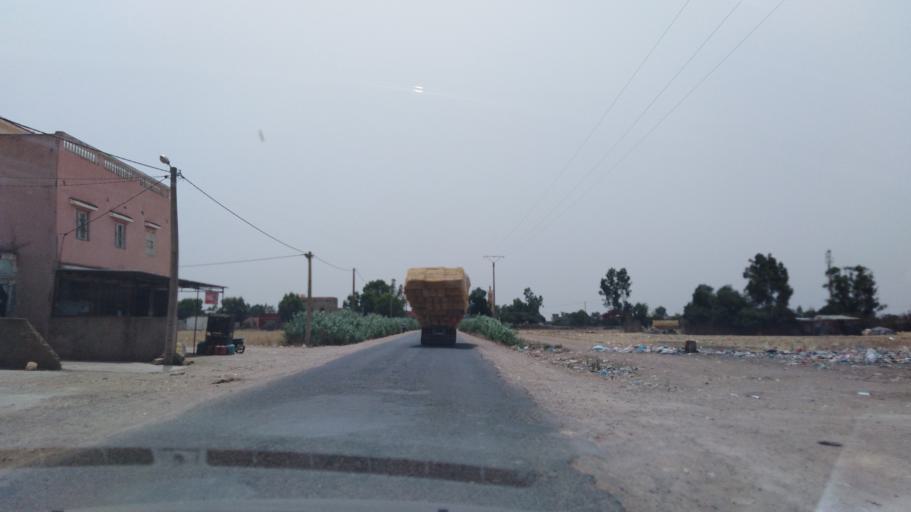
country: MA
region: Grand Casablanca
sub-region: Mediouna
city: Mediouna
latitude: 33.4024
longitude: -7.5127
